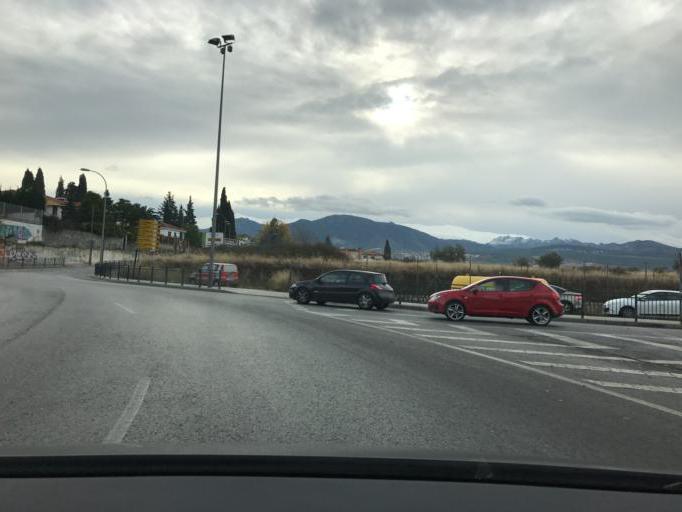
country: ES
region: Andalusia
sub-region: Provincia de Granada
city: Huetor Vega
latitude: 37.1551
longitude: -3.5853
